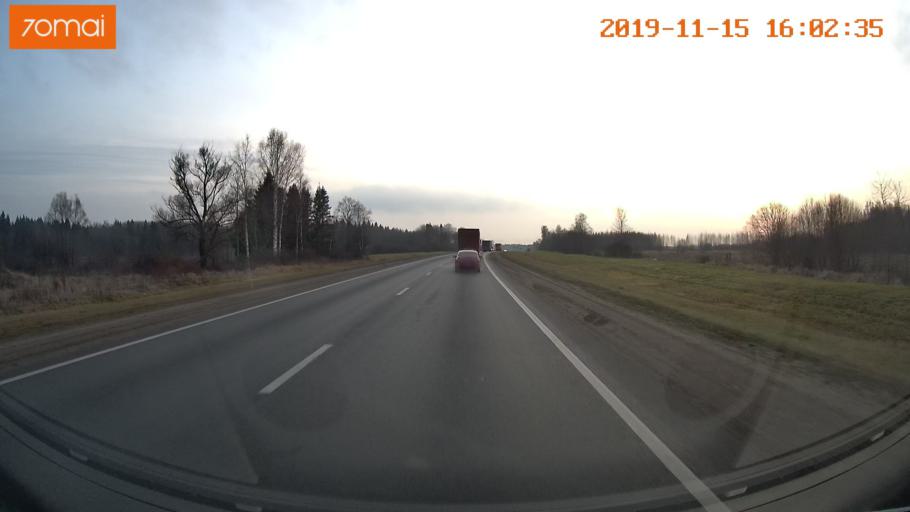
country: RU
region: Jaroslavl
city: Yaroslavl
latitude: 57.7697
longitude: 39.9234
